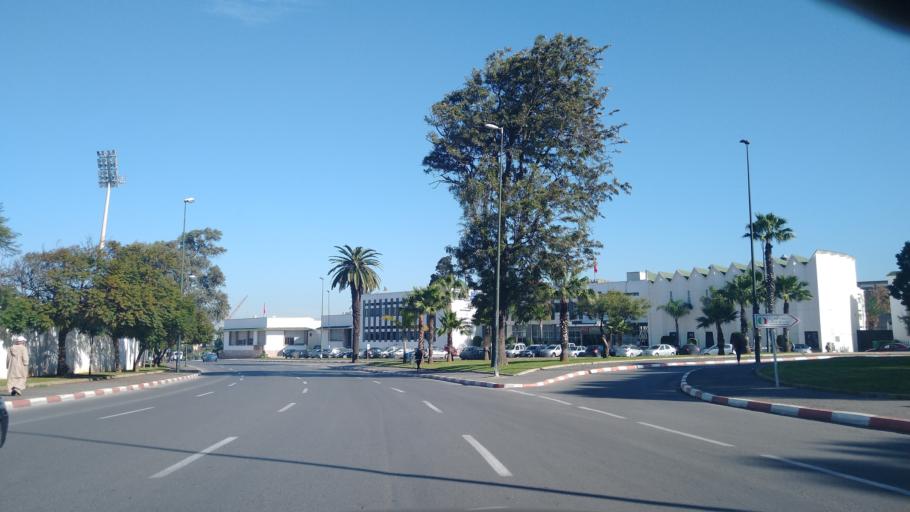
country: MA
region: Rabat-Sale-Zemmour-Zaer
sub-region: Rabat
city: Rabat
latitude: 34.0092
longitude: -6.8397
